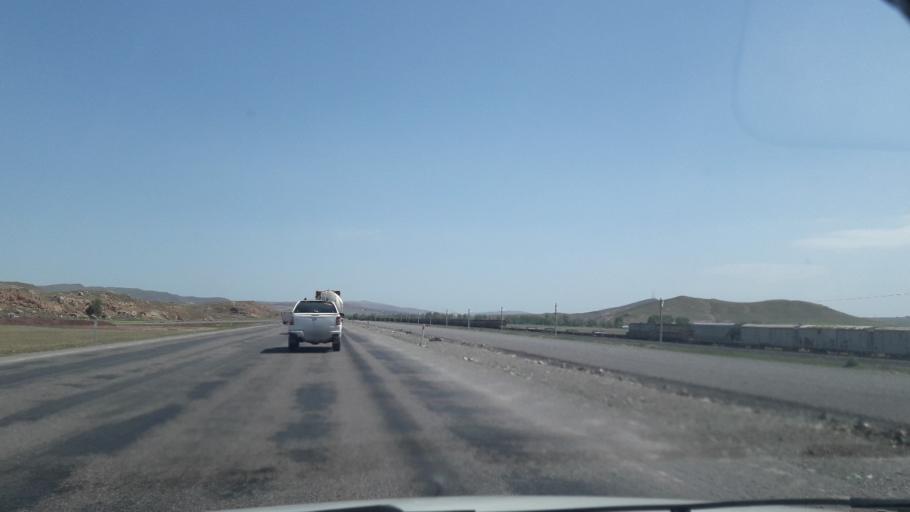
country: TR
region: Sivas
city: Ulas
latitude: 39.5369
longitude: 37.0194
